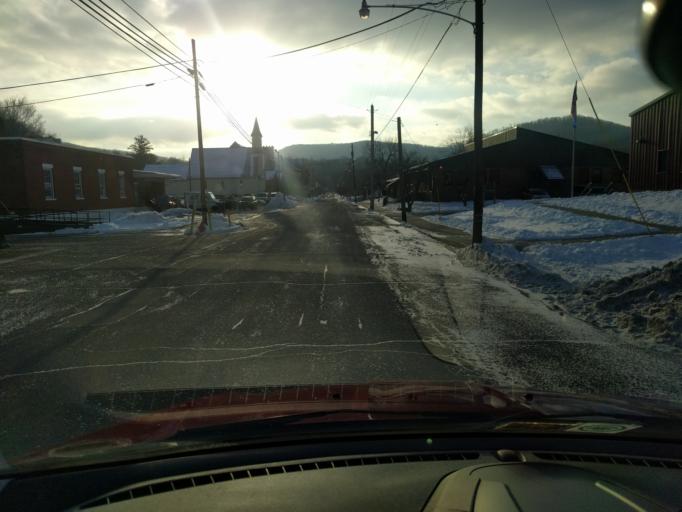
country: US
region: West Virginia
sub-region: Pocahontas County
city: Marlinton
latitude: 38.2215
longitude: -80.0940
